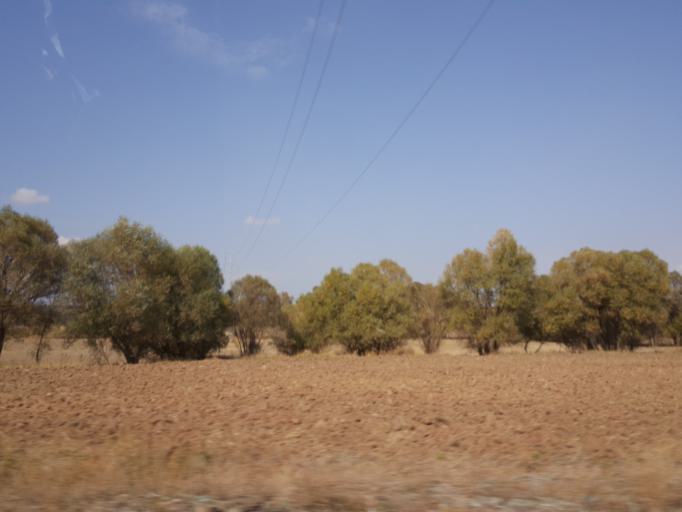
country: TR
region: Corum
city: Alaca
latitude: 40.1435
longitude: 34.8294
